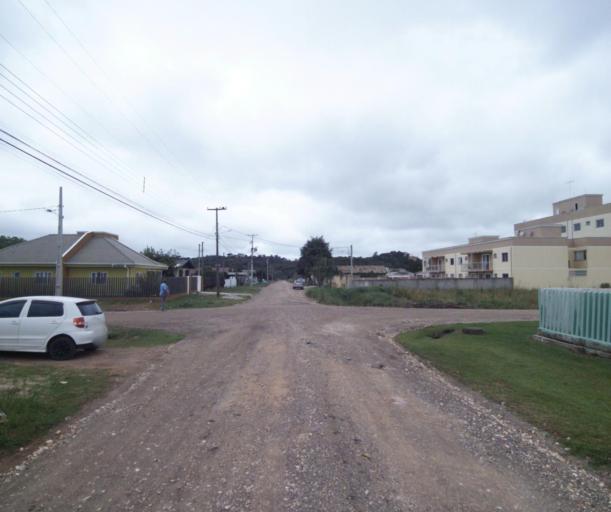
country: BR
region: Parana
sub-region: Quatro Barras
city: Quatro Barras
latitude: -25.3596
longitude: -49.0963
